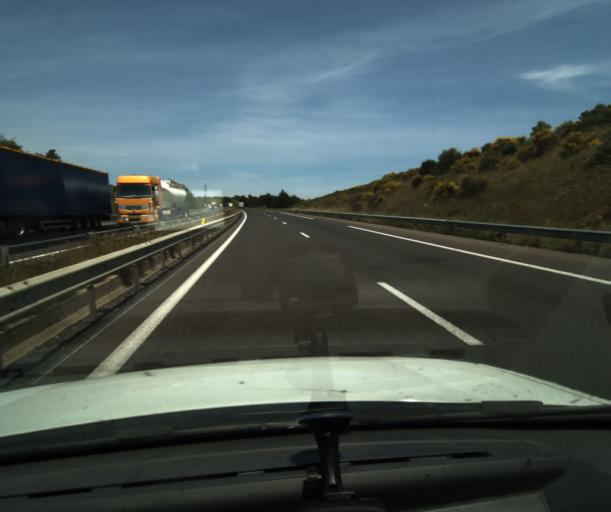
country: FR
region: Languedoc-Roussillon
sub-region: Departement des Pyrenees-Orientales
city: Banyuls-dels-Aspres
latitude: 42.5477
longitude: 2.8494
